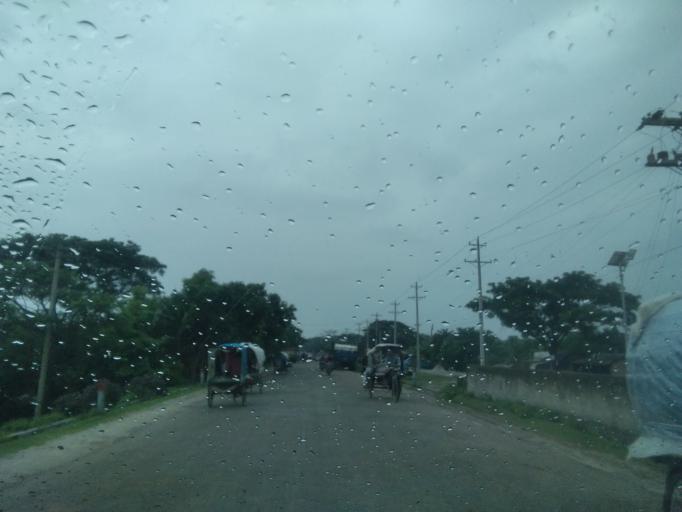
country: IN
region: West Bengal
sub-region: North 24 Parganas
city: Taki
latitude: 22.4568
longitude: 89.0340
